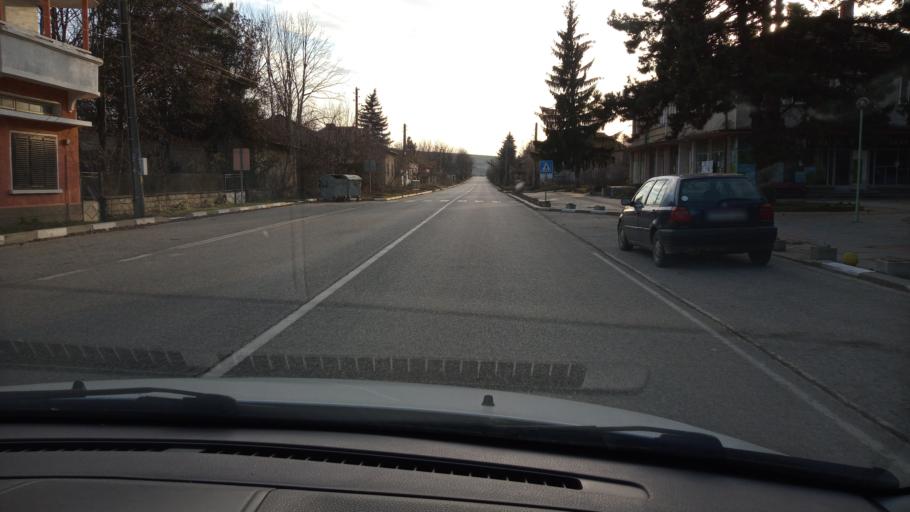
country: BG
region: Pleven
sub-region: Obshtina Pleven
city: Slavyanovo
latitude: 43.5536
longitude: 24.8651
